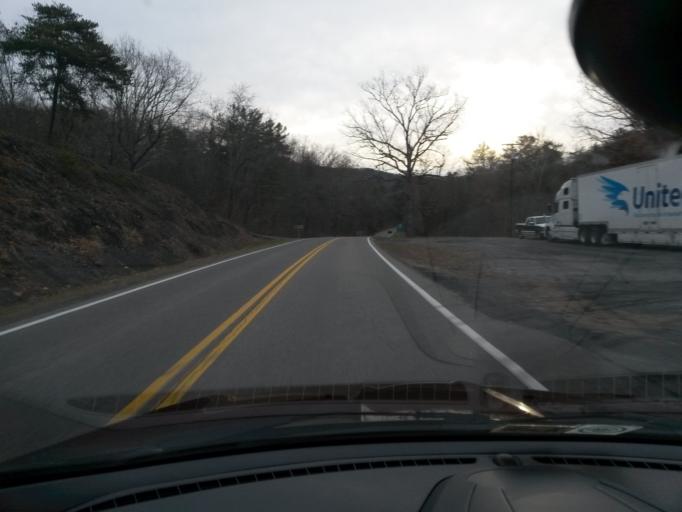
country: US
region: Virginia
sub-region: Alleghany County
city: Clifton Forge
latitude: 37.8275
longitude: -79.7596
